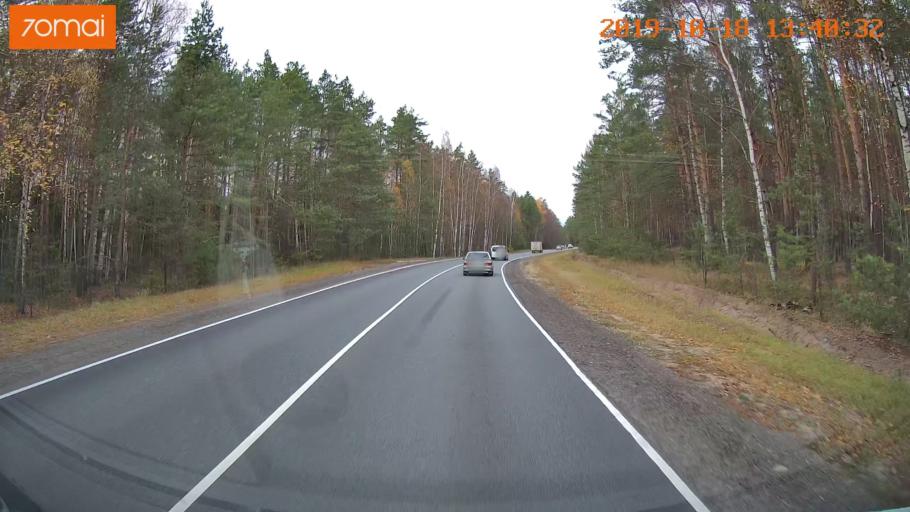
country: RU
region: Rjazan
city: Solotcha
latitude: 54.9106
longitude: 39.9980
